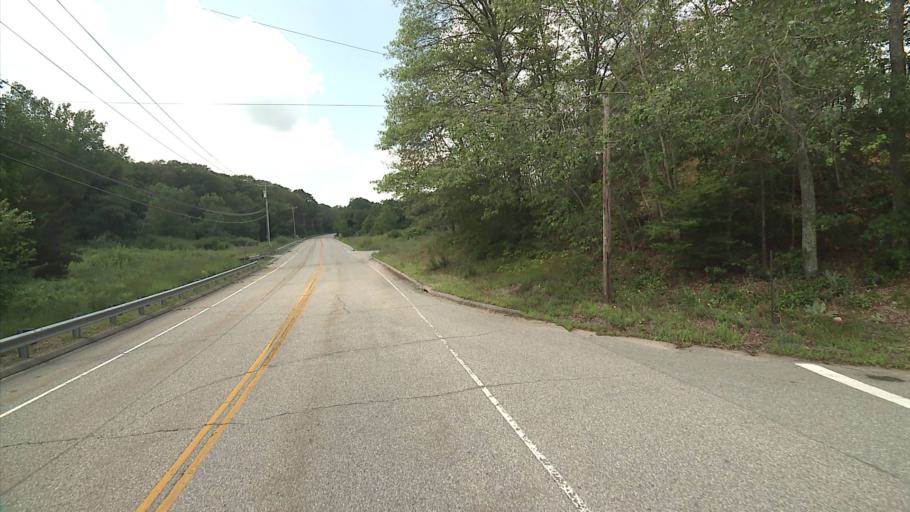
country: US
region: Connecticut
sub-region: New London County
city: Lisbon
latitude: 41.6152
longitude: -72.0425
